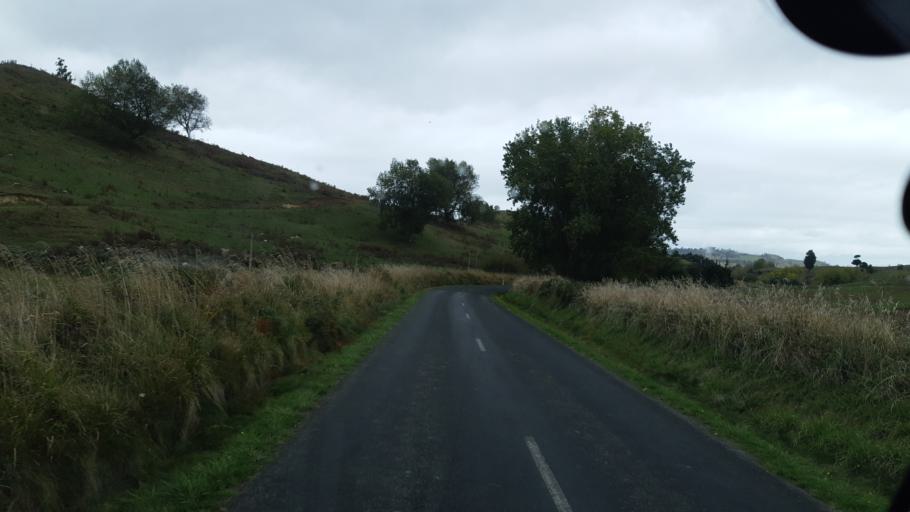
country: NZ
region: Manawatu-Wanganui
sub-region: Ruapehu District
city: Waiouru
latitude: -39.5552
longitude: 175.6171
